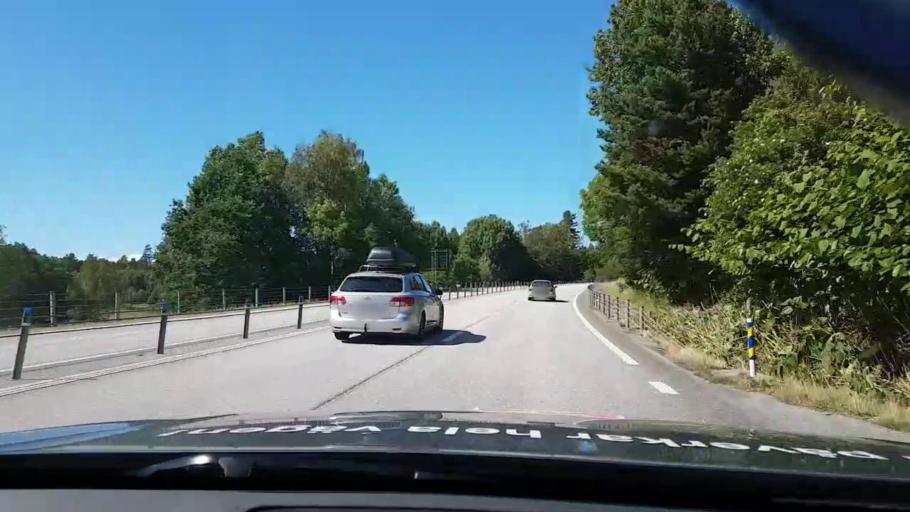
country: SE
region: Kalmar
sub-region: Vasterviks Kommun
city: Gamleby
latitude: 57.8529
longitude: 16.4302
